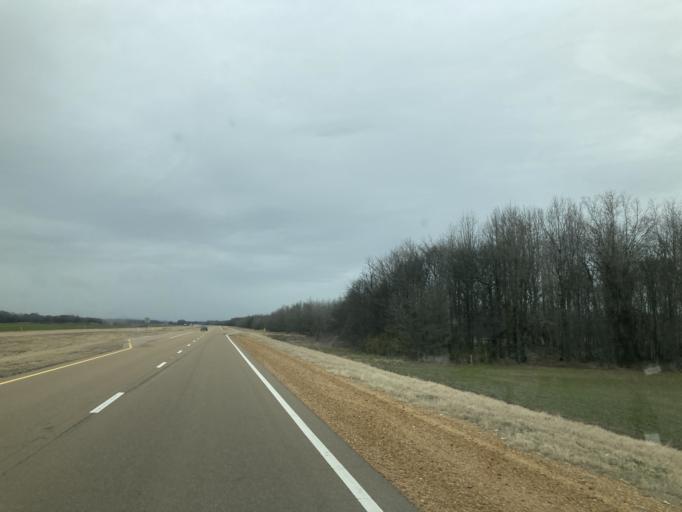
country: US
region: Mississippi
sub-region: Yazoo County
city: Yazoo City
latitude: 33.0133
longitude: -90.4690
